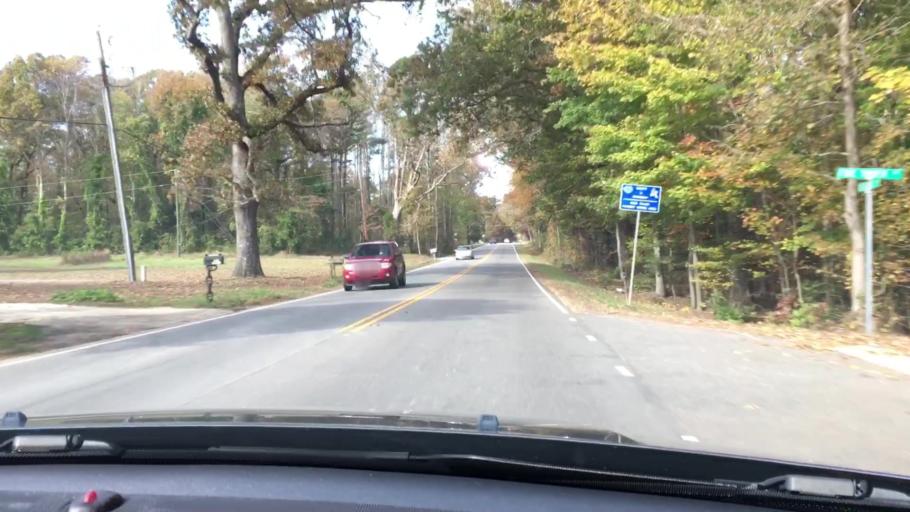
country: US
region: Virginia
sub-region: King William County
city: West Point
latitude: 37.4329
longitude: -76.8330
